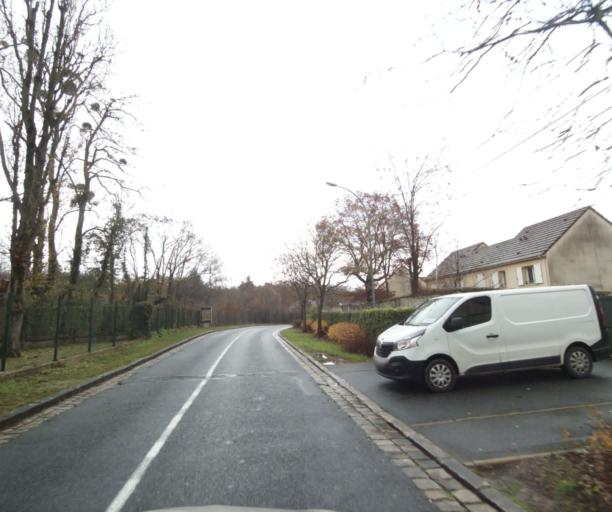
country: FR
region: Ile-de-France
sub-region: Departement de Seine-et-Marne
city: Avon
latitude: 48.4195
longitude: 2.7294
